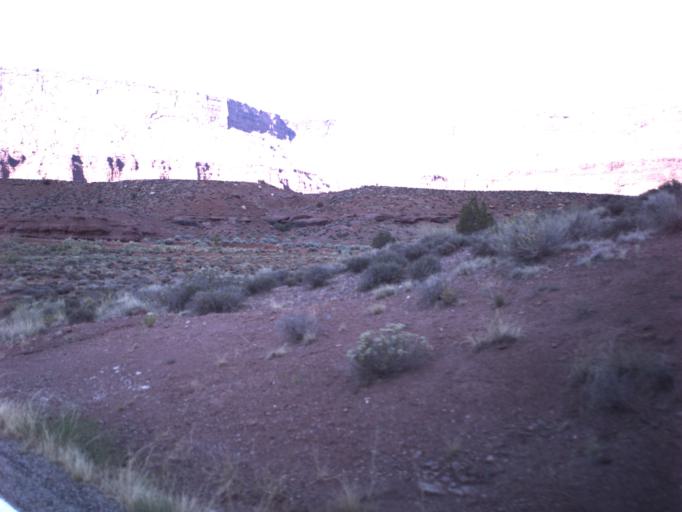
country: US
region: Utah
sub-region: Grand County
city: Moab
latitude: 38.7480
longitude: -109.3300
